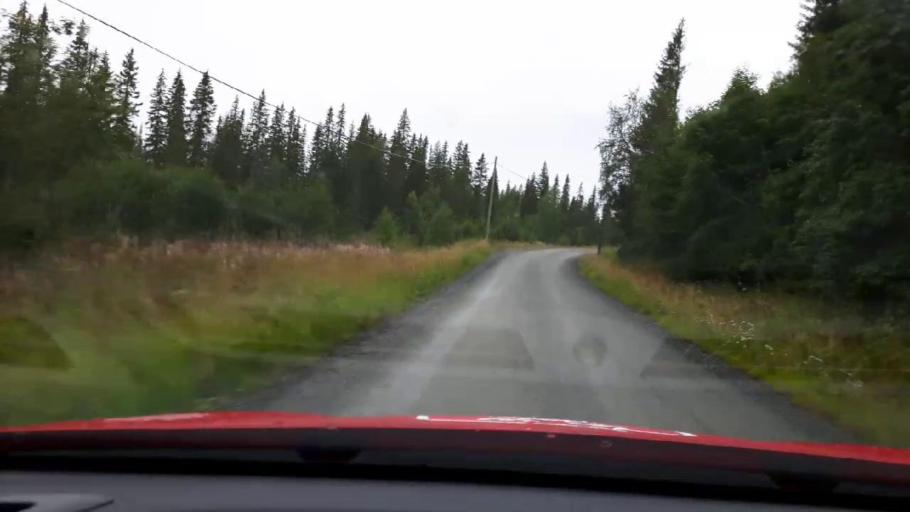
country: SE
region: Jaemtland
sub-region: Are Kommun
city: Are
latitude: 63.5010
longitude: 12.7554
